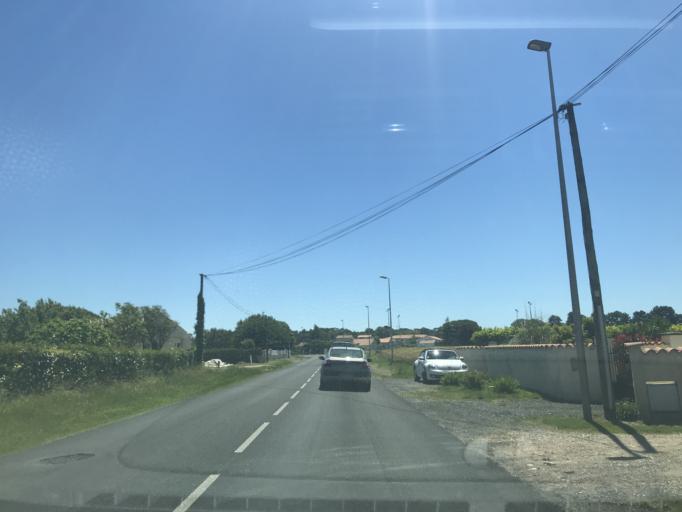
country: FR
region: Poitou-Charentes
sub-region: Departement de la Charente-Maritime
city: Meschers-sur-Gironde
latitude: 45.5746
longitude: -0.9608
